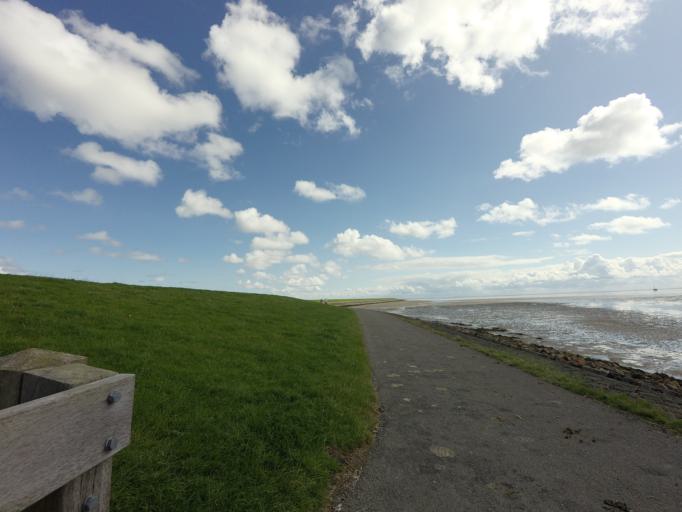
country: NL
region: Friesland
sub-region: Gemeente Terschelling
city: West-Terschelling
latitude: 53.3729
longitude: 5.2576
